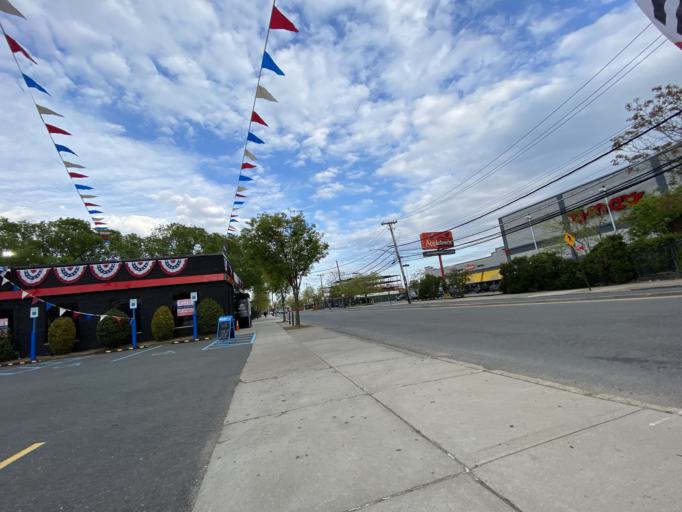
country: US
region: New York
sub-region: Richmond County
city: Staten Island
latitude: 40.5702
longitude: -74.1090
